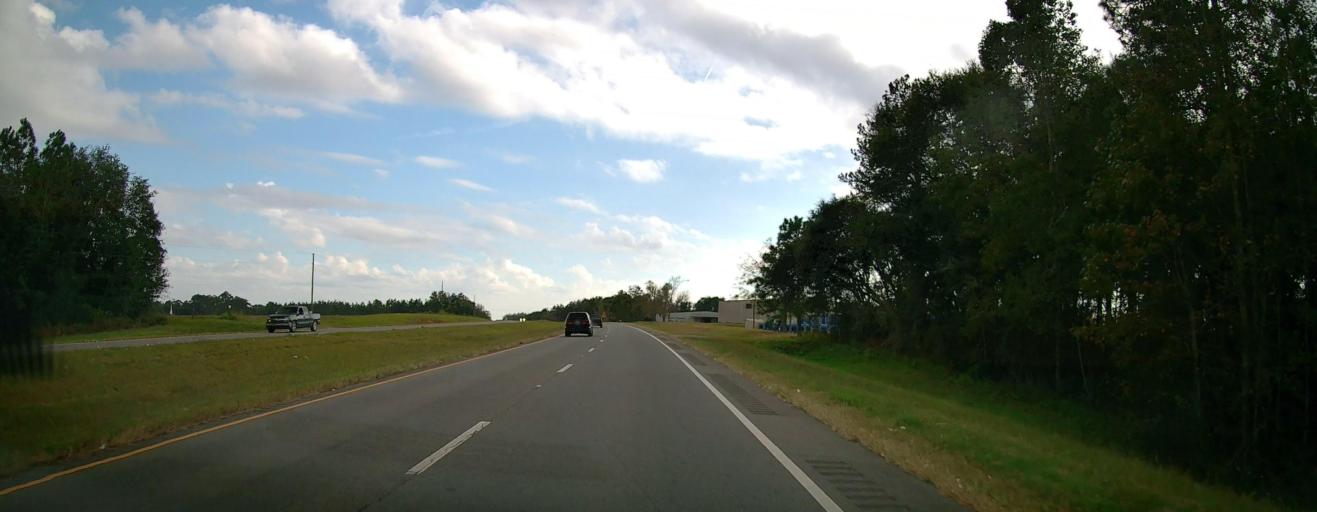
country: US
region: Georgia
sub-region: Thomas County
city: Meigs
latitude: 31.0482
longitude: -84.0707
